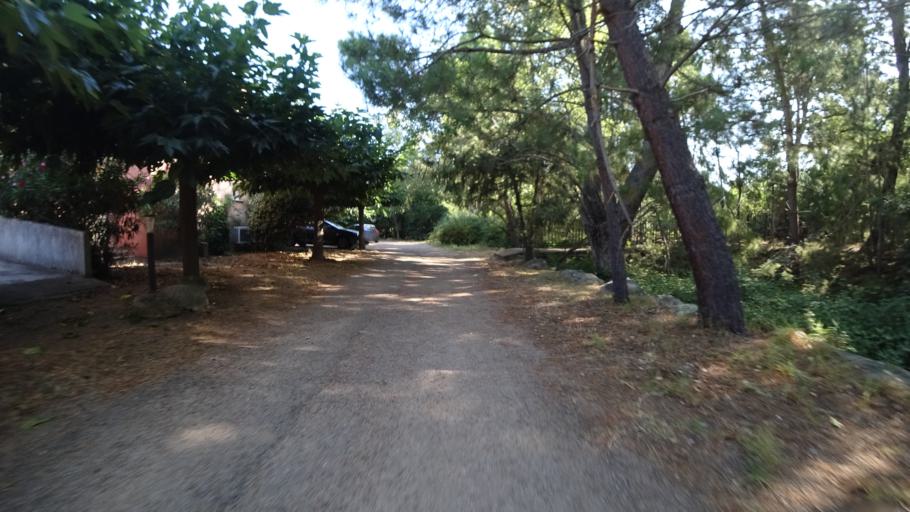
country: FR
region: Corsica
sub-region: Departement de la Corse-du-Sud
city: Porto-Vecchio
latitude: 41.6332
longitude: 9.3342
